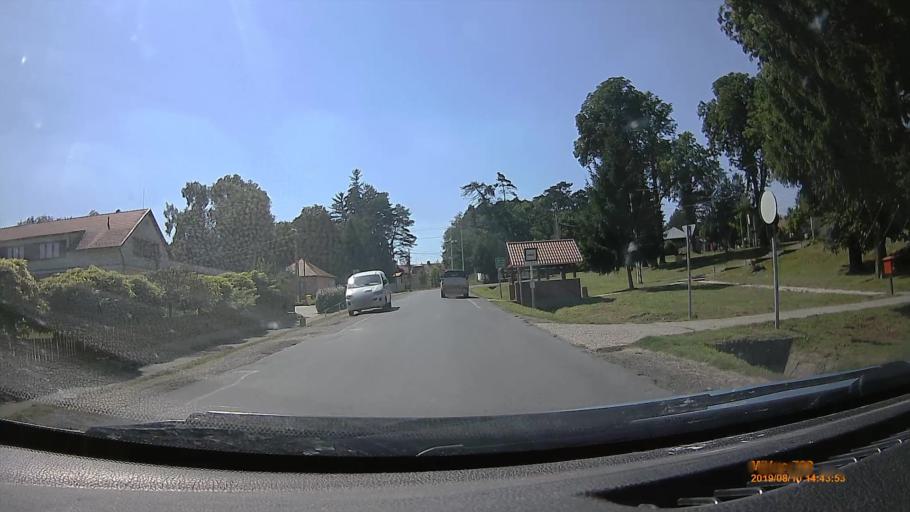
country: HU
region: Somogy
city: Somogyvar
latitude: 46.5799
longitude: 17.6504
